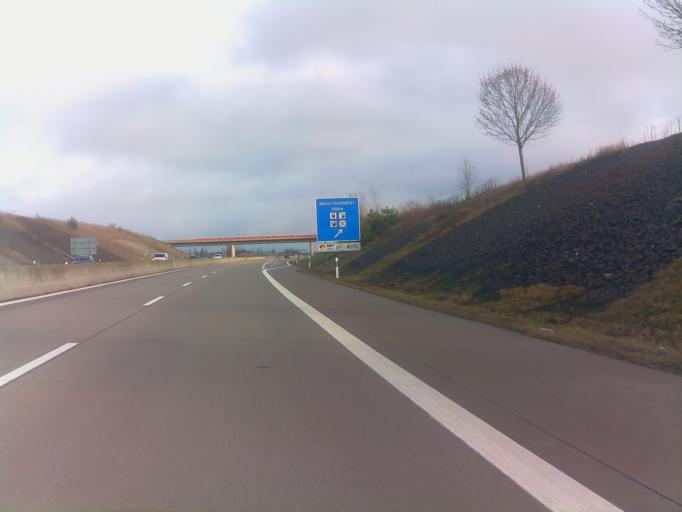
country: DE
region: Bavaria
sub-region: Regierungsbezirk Unterfranken
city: Hendungen
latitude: 50.4179
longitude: 10.3393
